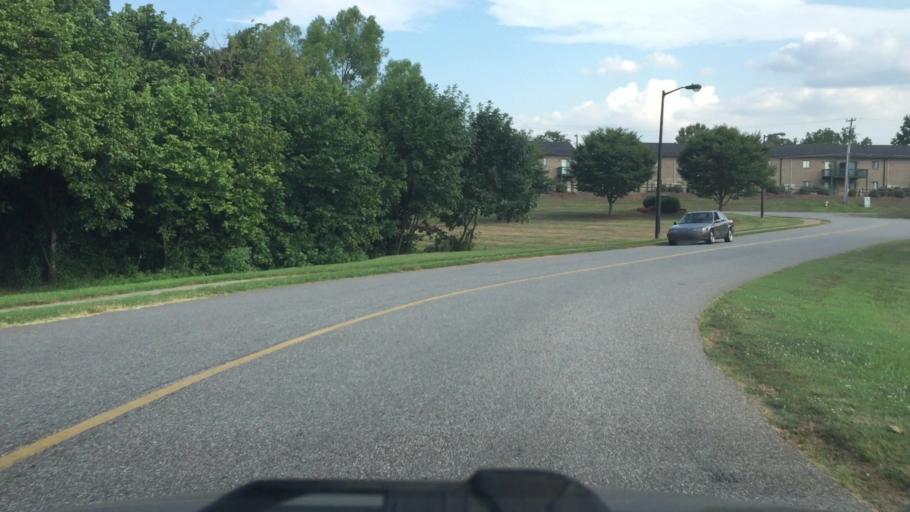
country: US
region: North Carolina
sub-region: Iredell County
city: Statesville
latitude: 35.8016
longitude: -80.8528
